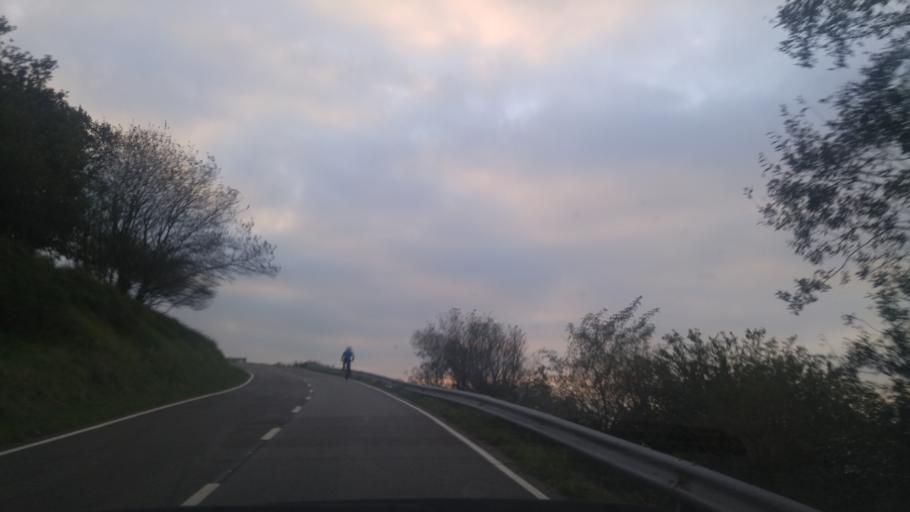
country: ES
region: Asturias
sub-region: Province of Asturias
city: Oviedo
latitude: 43.3881
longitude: -5.8529
